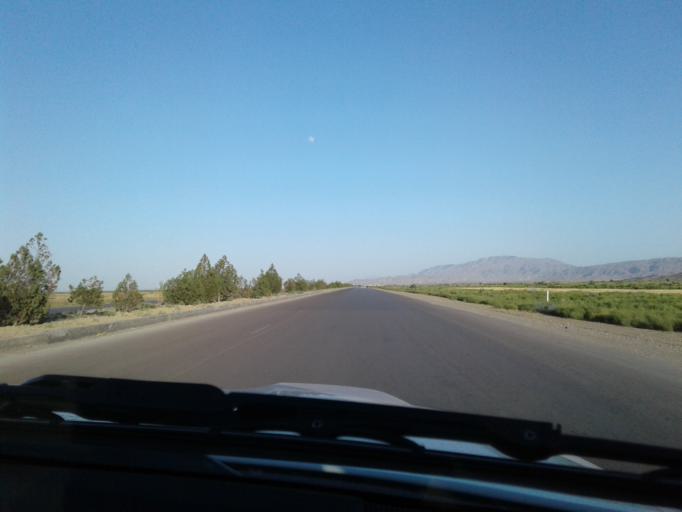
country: TM
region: Ahal
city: Baharly
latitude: 38.3671
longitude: 57.5225
